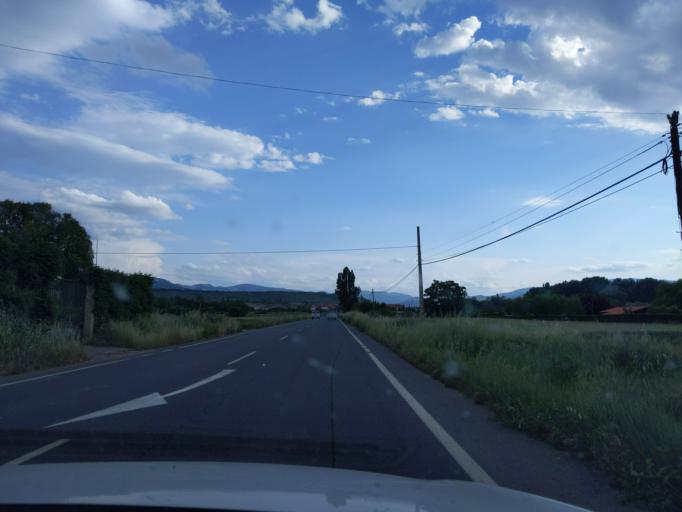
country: ES
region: La Rioja
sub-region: Provincia de La Rioja
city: Alberite
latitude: 42.4173
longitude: -2.4321
